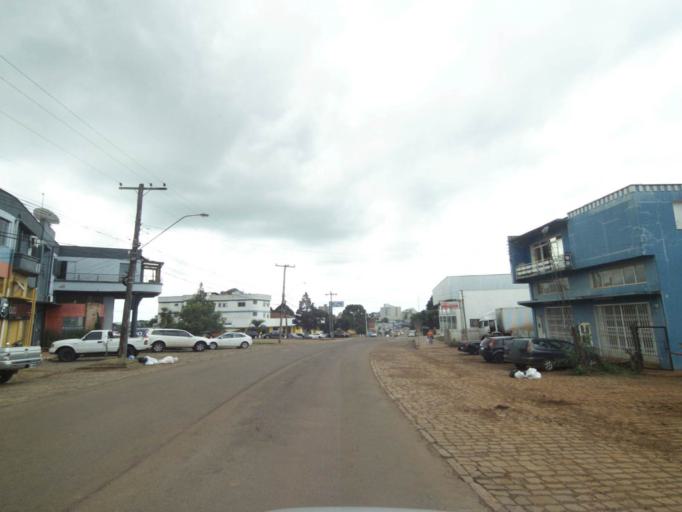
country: BR
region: Rio Grande do Sul
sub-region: Lagoa Vermelha
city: Lagoa Vermelha
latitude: -28.2165
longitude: -51.5187
